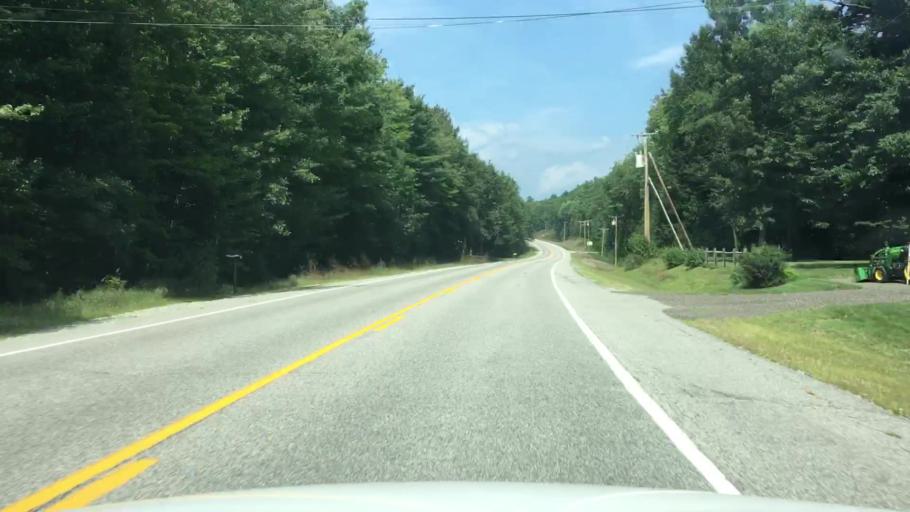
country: US
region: Maine
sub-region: Oxford County
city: Canton
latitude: 44.4744
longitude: -70.3268
